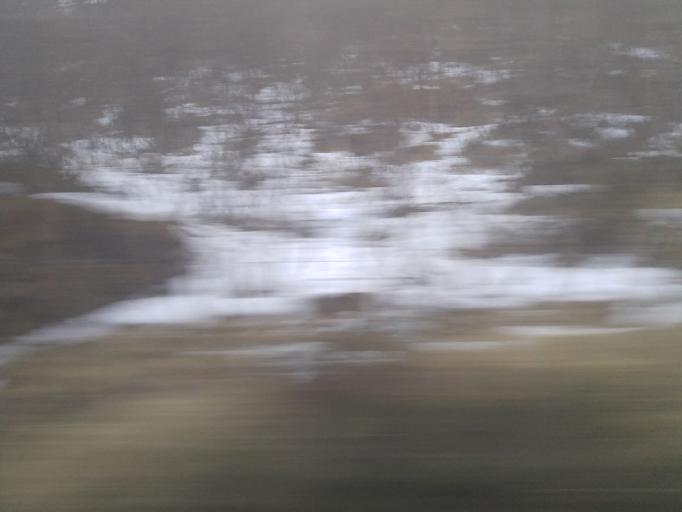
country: NO
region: Sor-Trondelag
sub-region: Oppdal
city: Oppdal
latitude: 62.3199
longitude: 9.6175
